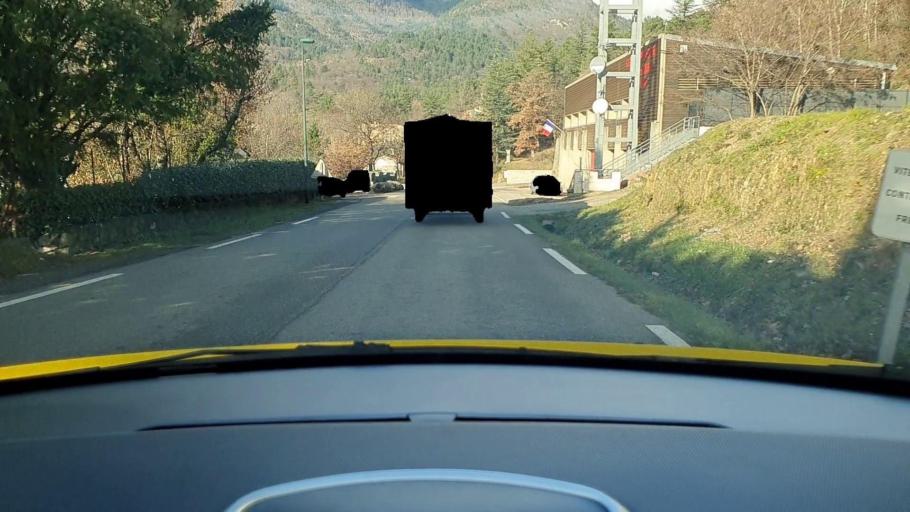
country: FR
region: Languedoc-Roussillon
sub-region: Departement du Gard
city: Branoux-les-Taillades
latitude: 44.3525
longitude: 3.9526
